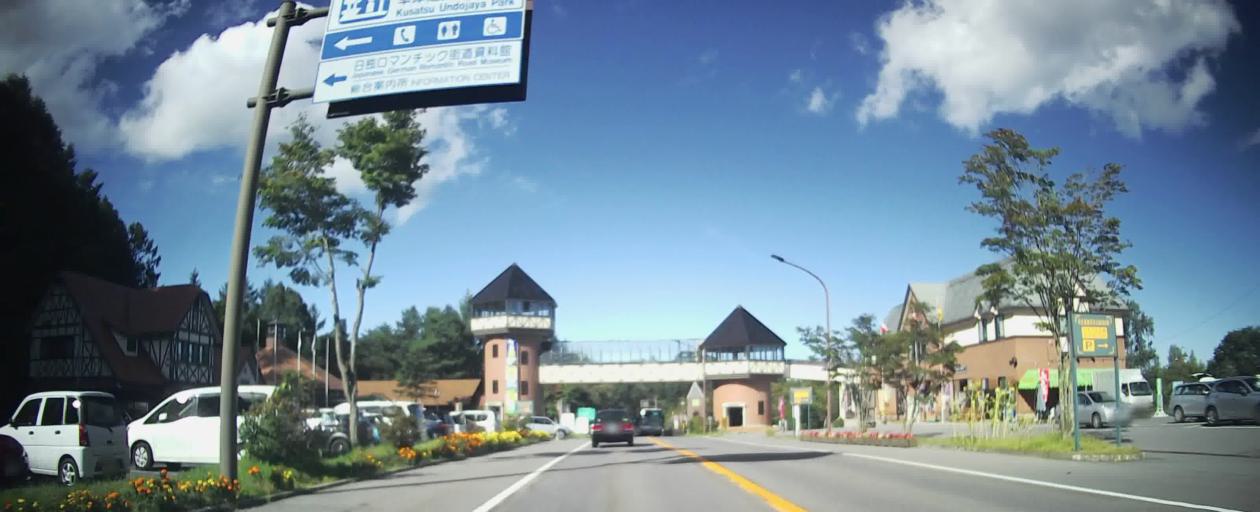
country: JP
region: Gunma
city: Nakanojomachi
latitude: 36.6144
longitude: 138.5901
